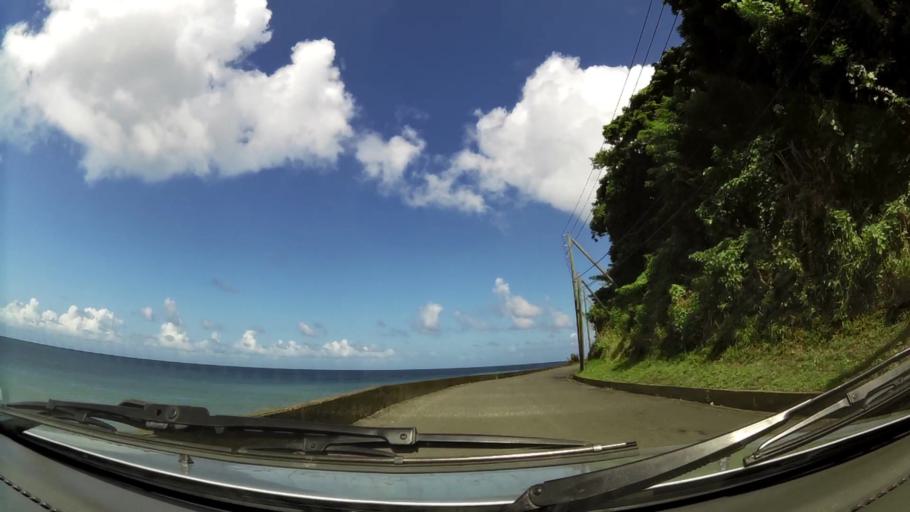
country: GD
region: Saint Mark
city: Victoria
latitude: 12.1890
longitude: -61.7183
